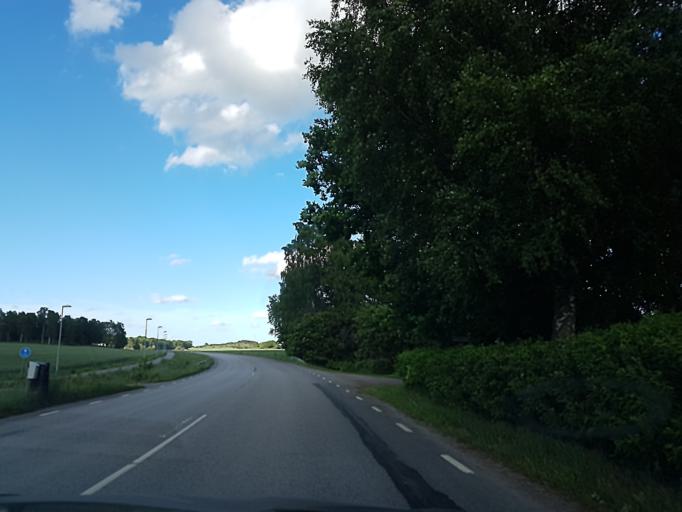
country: SE
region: Soedermanland
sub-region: Nykopings Kommun
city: Nykoping
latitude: 58.7415
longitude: 16.9481
